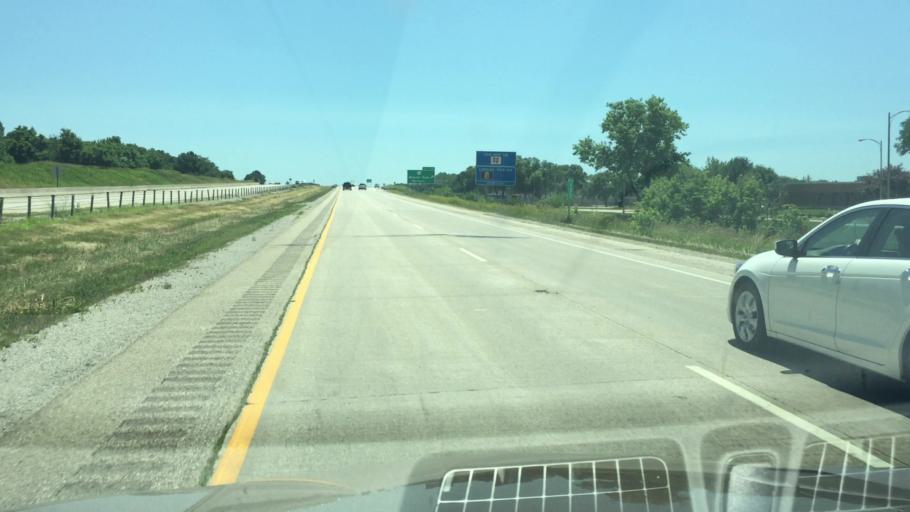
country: US
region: Wisconsin
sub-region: Dodge County
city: Beaver Dam
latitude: 43.4626
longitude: -88.8153
